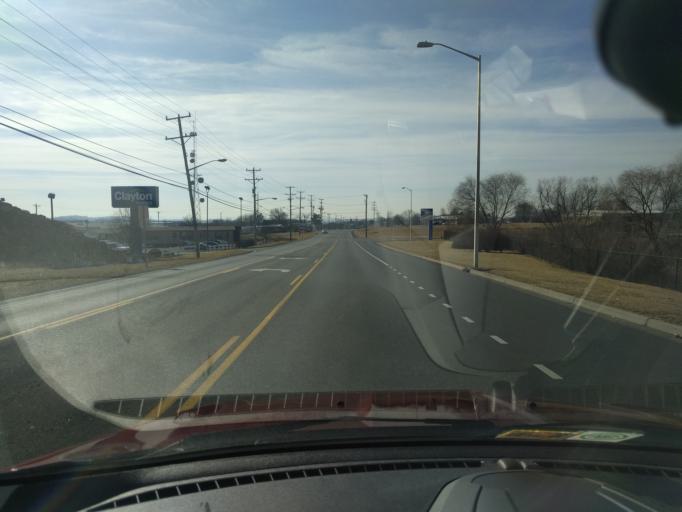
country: US
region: Virginia
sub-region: Rockingham County
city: Dayton
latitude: 38.3979
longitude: -78.9140
